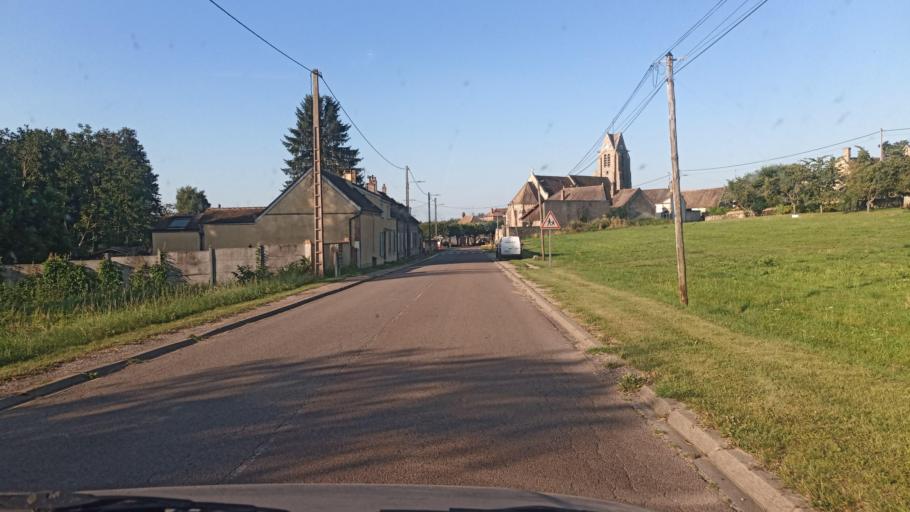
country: FR
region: Bourgogne
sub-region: Departement de l'Yonne
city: Saint-Valerien
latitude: 48.2321
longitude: 3.1191
